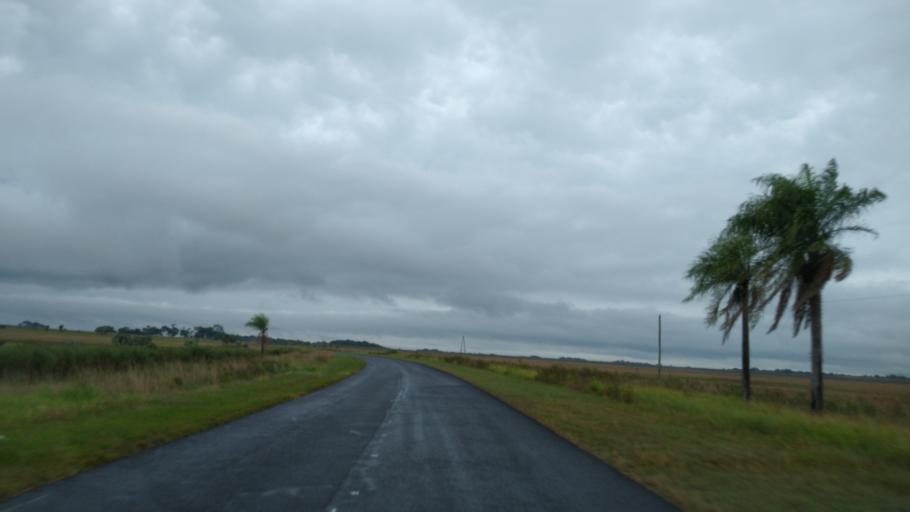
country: AR
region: Corrientes
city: Loreto
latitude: -27.7196
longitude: -57.2306
